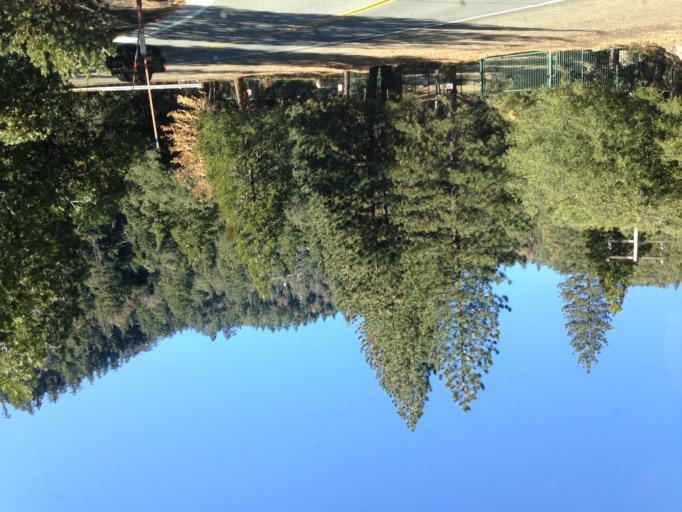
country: US
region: California
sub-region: Riverside County
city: Idyllwild-Pine Cove
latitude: 33.7772
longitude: -116.7365
